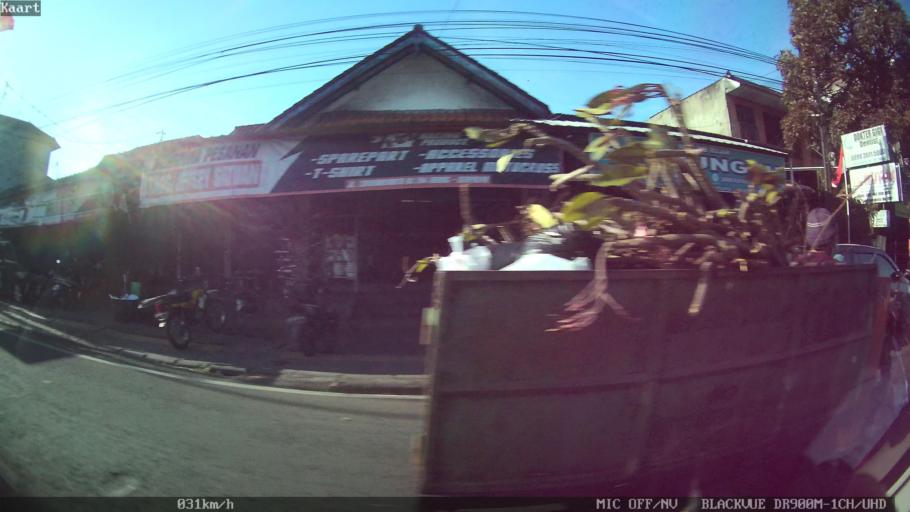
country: ID
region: Bali
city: Banjar Kertasari
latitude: -8.6325
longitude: 115.2058
